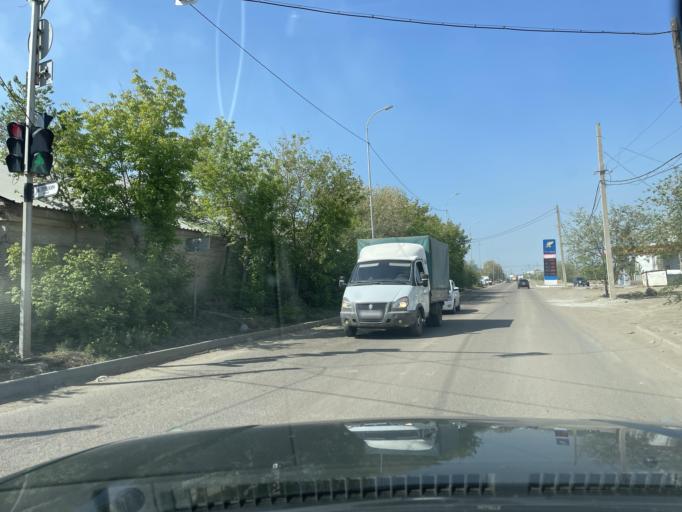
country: KZ
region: Qaraghandy
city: Zhezqazghan
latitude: 47.7877
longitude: 67.7142
